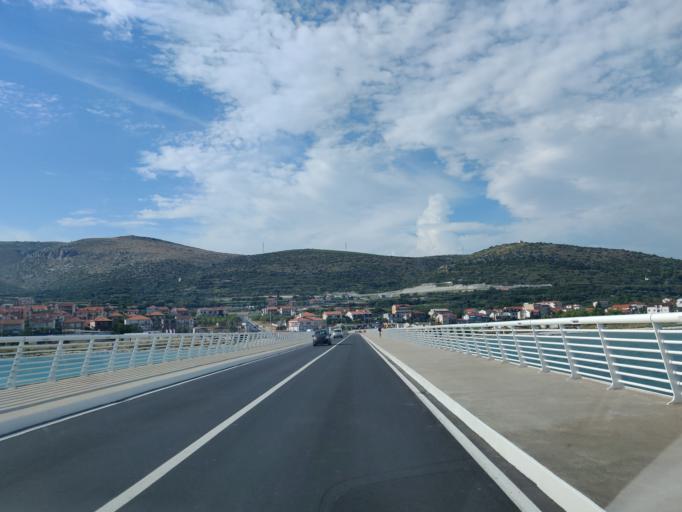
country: HR
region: Splitsko-Dalmatinska
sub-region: Grad Trogir
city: Trogir
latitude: 43.5194
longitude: 16.2650
